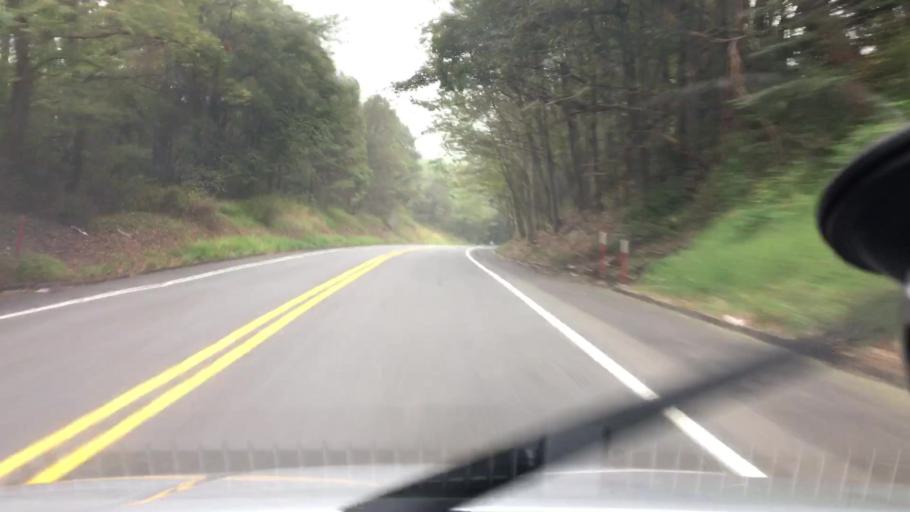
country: US
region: Pennsylvania
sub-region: Monroe County
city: Mount Pocono
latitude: 41.1285
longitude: -75.3404
